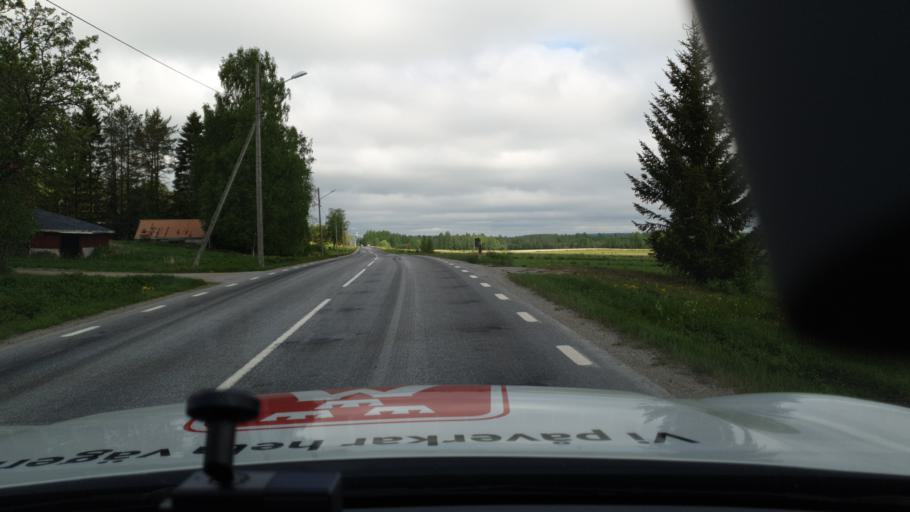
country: SE
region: Vaesterbotten
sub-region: Umea Kommun
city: Roback
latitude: 63.9176
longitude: 20.1943
